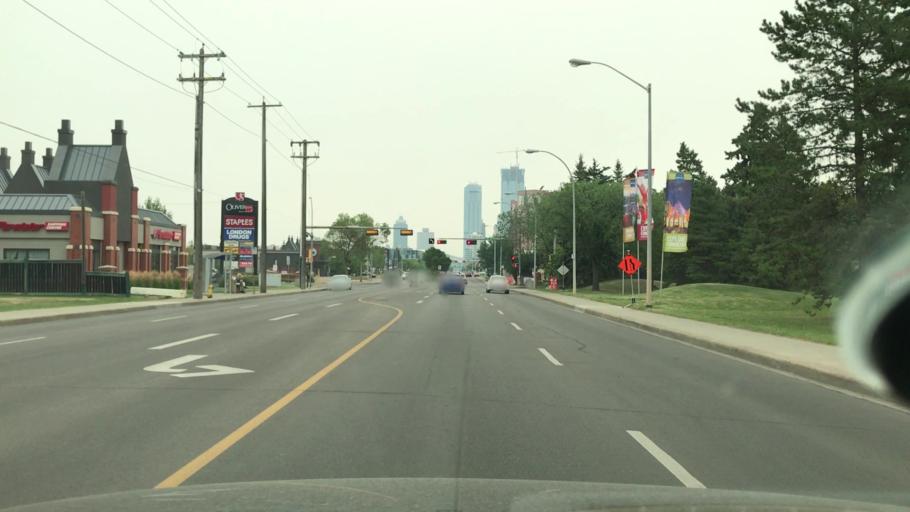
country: CA
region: Alberta
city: Edmonton
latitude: 53.5462
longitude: -113.5264
